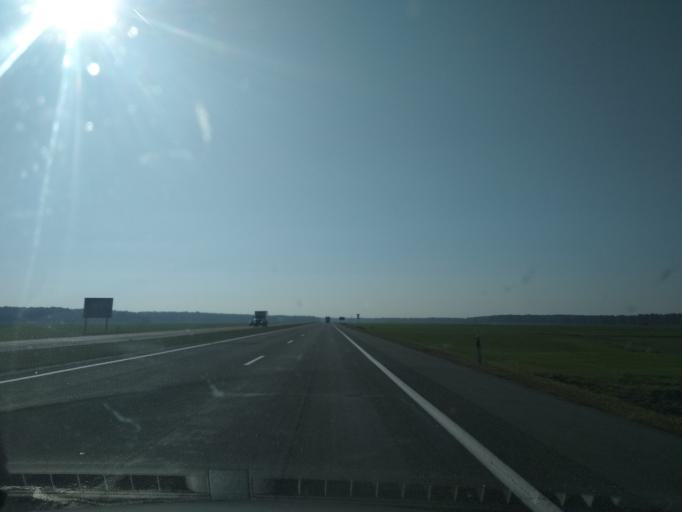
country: BY
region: Brest
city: Antopal'
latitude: 52.3028
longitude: 24.5903
